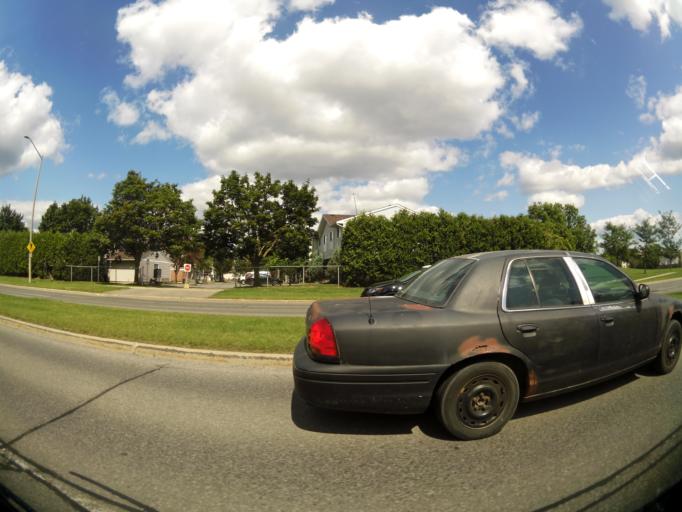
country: CA
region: Quebec
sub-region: Outaouais
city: Gatineau
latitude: 45.4590
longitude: -75.5086
